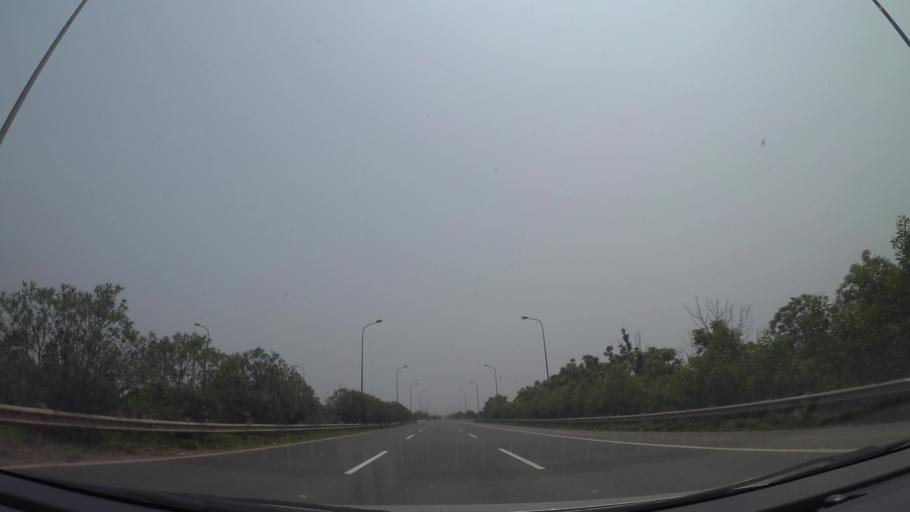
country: VN
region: Ha Noi
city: Quoc Oai
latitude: 20.9949
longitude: 105.5896
